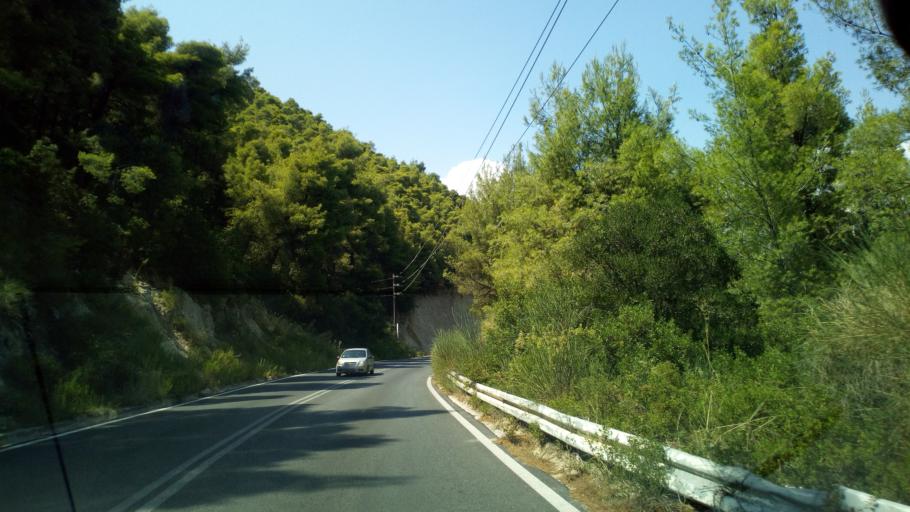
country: GR
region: Central Macedonia
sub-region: Nomos Chalkidikis
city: Agios Nikolaos
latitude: 40.2094
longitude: 23.7582
